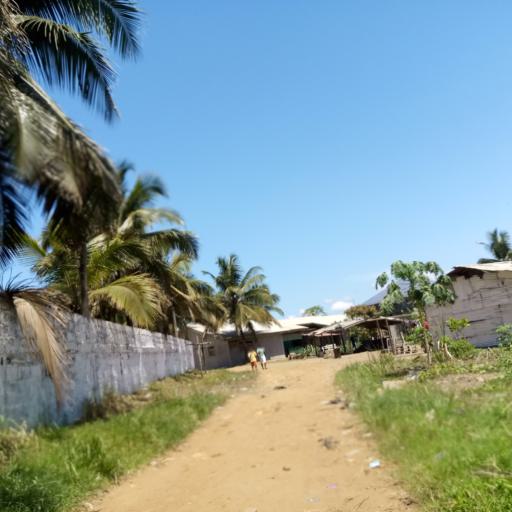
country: LR
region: Montserrado
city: Monrovia
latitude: 6.2352
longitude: -10.6946
